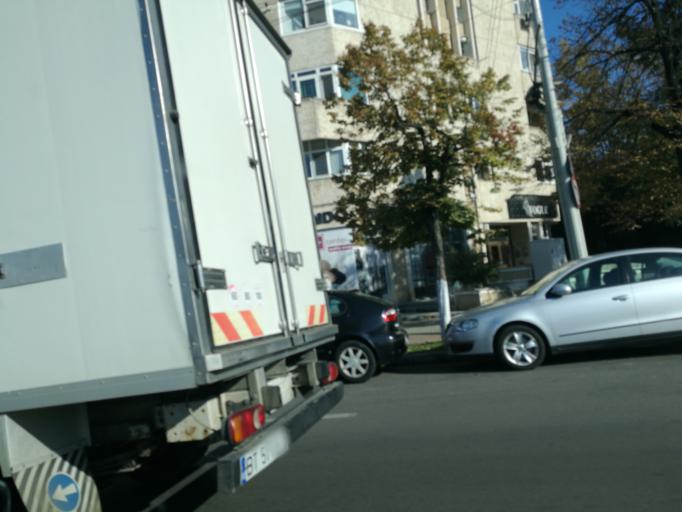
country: RO
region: Iasi
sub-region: Municipiul Iasi
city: Iasi
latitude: 47.1734
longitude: 27.5603
